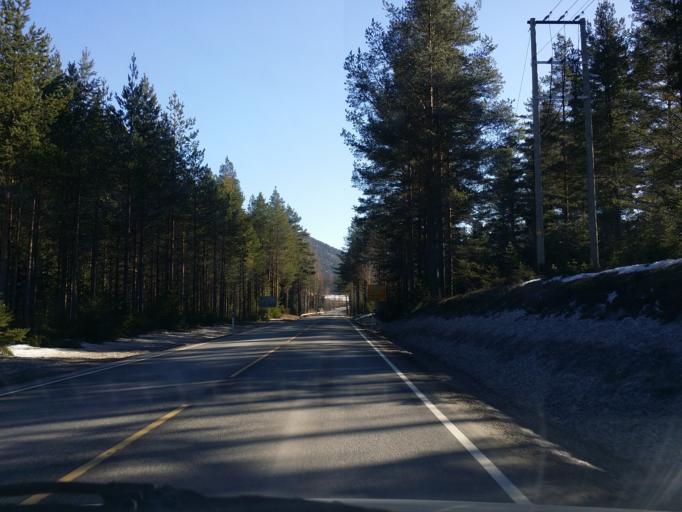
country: NO
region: Buskerud
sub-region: Ringerike
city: Honefoss
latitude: 60.3539
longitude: 10.0987
